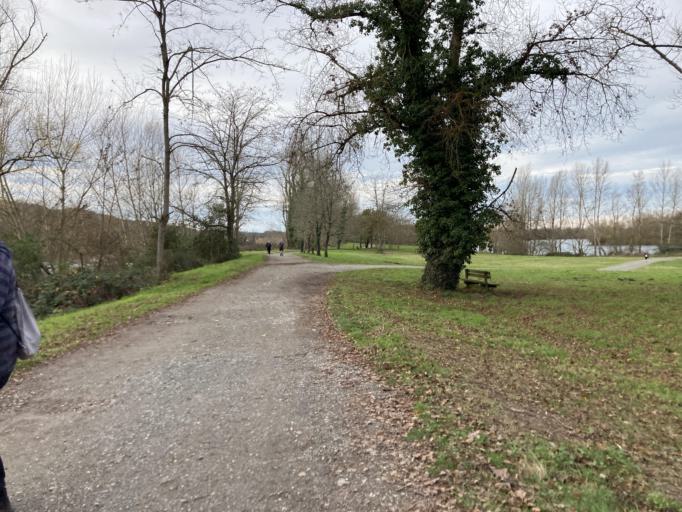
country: FR
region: Aquitaine
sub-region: Departement des Pyrenees-Atlantiques
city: Artiguelouve
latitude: 43.3072
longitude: -0.4384
